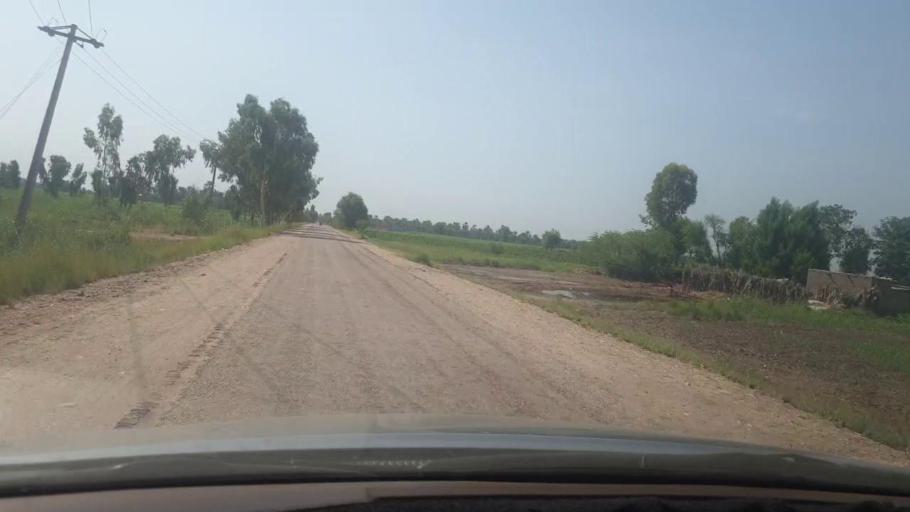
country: PK
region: Sindh
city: Ranipur
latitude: 27.2910
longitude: 68.5756
